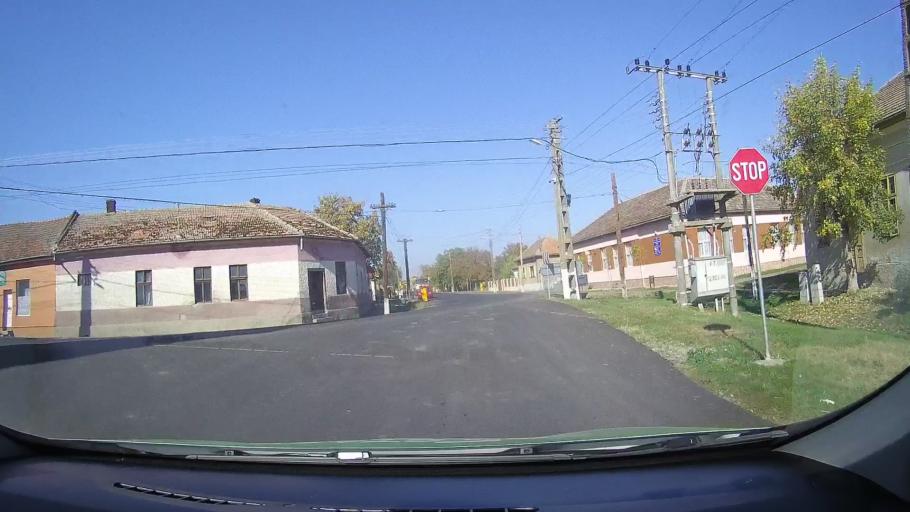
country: RO
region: Satu Mare
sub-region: Comuna Tiream
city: Tiream
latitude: 47.6154
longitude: 22.4722
